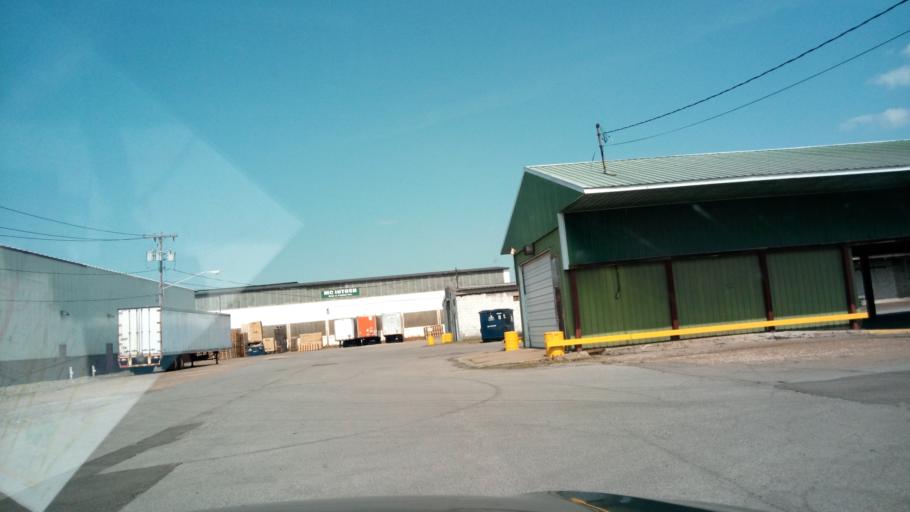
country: US
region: New York
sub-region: Erie County
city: West Seneca
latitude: 42.8716
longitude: -78.8226
